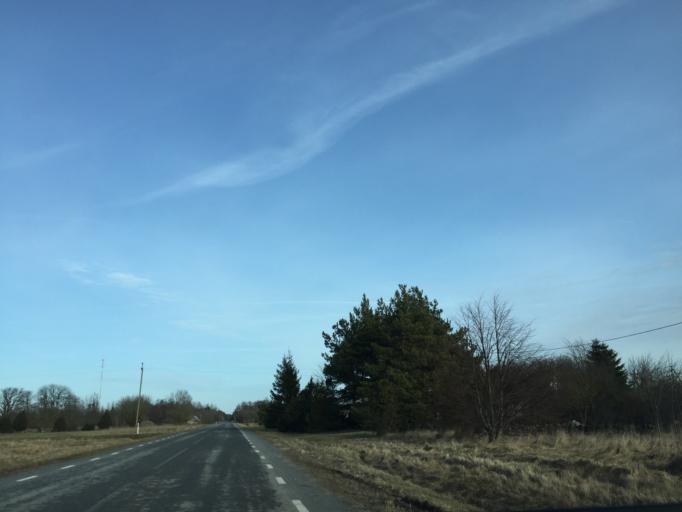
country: EE
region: Saare
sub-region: Kuressaare linn
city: Kuressaare
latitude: 58.2668
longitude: 21.9105
